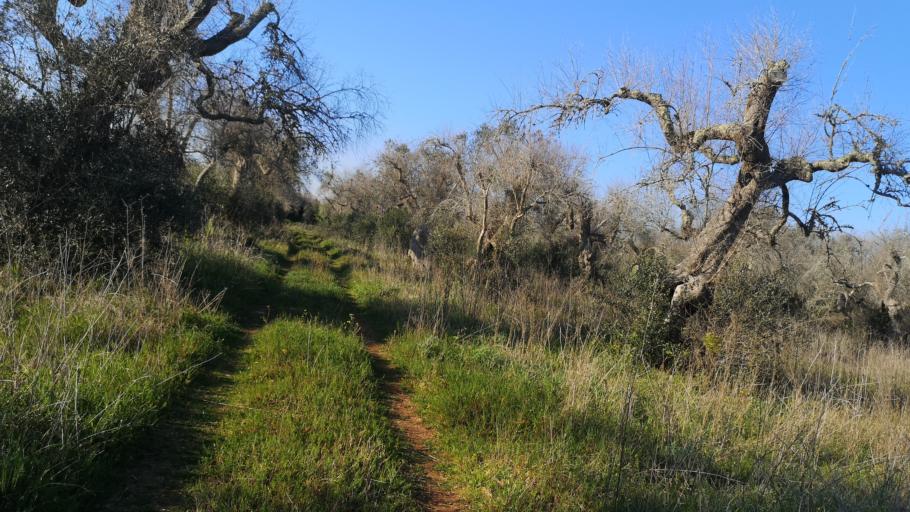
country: IT
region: Apulia
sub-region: Provincia di Lecce
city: Surano
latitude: 40.0072
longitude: 18.3393
